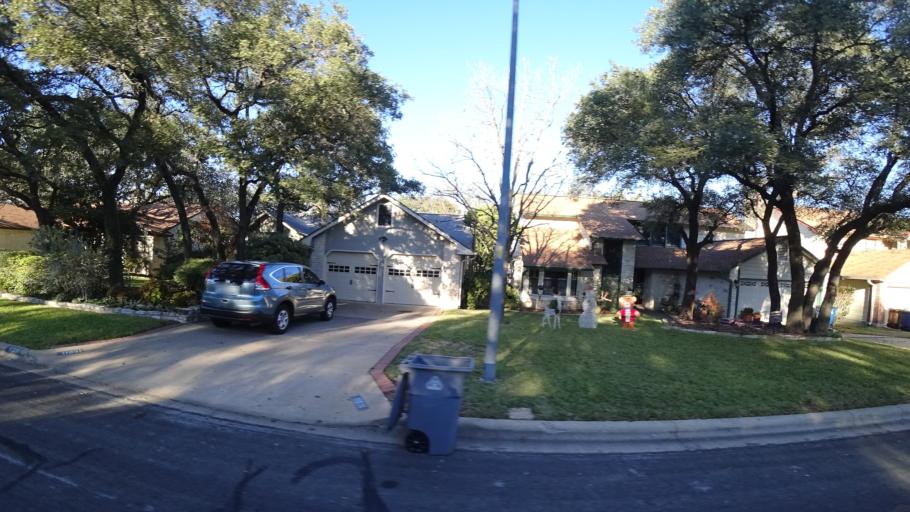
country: US
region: Texas
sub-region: Travis County
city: Wells Branch
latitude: 30.3986
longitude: -97.6972
